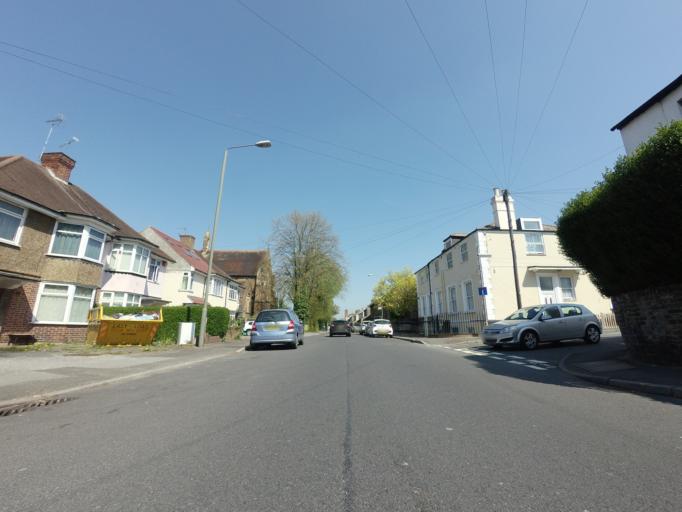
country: GB
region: England
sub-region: Greater London
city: Orpington
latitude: 51.3840
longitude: 0.1092
